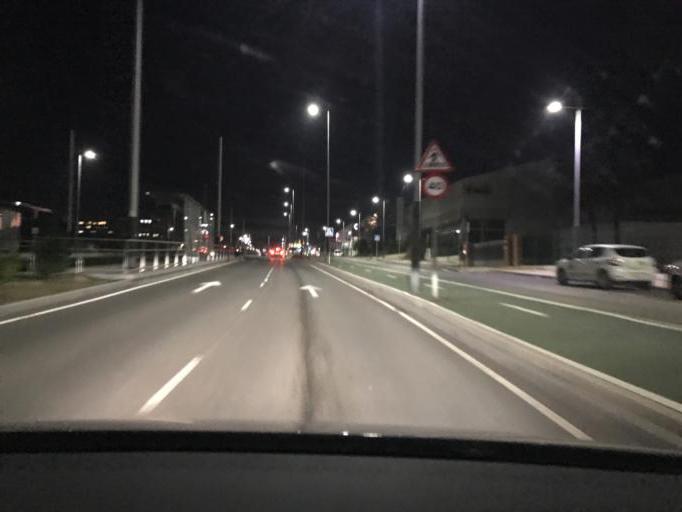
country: ES
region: Andalusia
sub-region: Provincia de Jaen
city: Jaen
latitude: 37.8000
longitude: -3.7785
